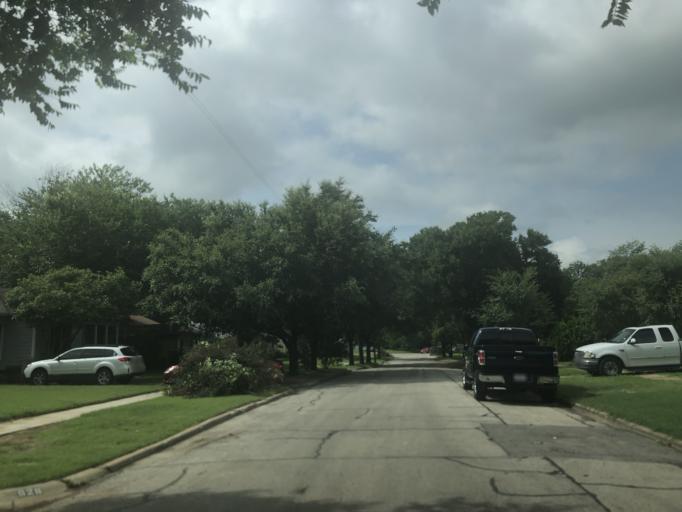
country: US
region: Texas
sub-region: Dallas County
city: Irving
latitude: 32.8076
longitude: -96.9601
